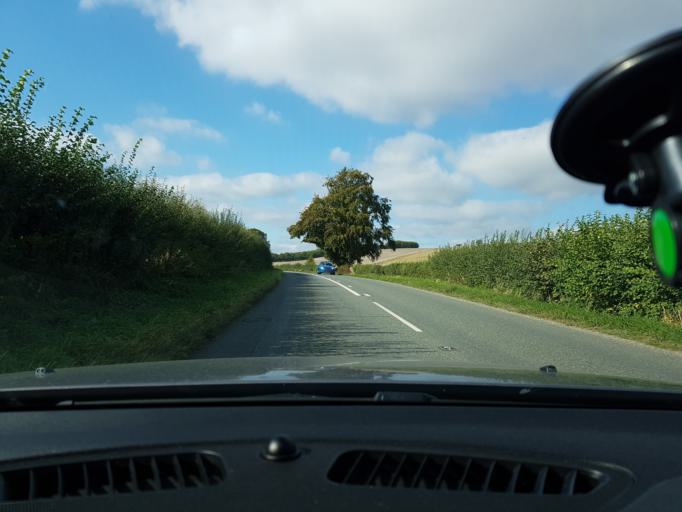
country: GB
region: England
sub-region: Wiltshire
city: Aldbourne
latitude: 51.4866
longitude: -1.6368
